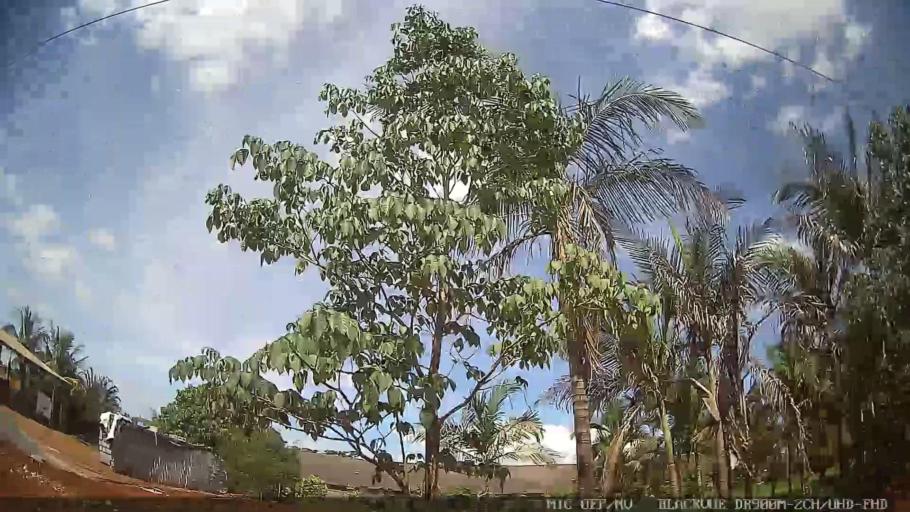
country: BR
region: Sao Paulo
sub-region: Artur Nogueira
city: Artur Nogueira
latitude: -22.6031
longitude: -47.0718
